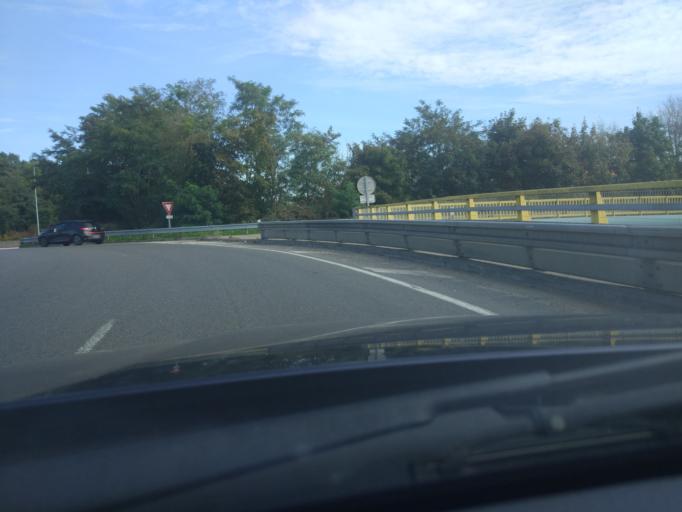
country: FR
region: Ile-de-France
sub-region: Departement de l'Essonne
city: Arpajon
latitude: 48.5980
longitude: 2.2448
